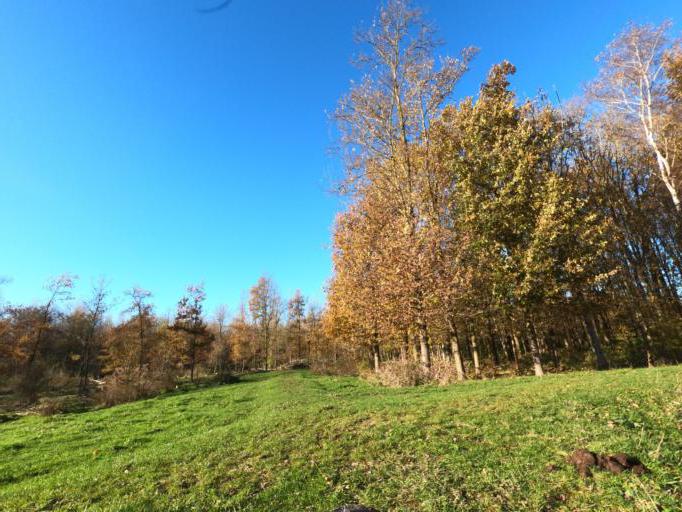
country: NL
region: Gelderland
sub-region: Gemeente Nijkerk
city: Nijkerk
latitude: 52.2629
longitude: 5.4432
